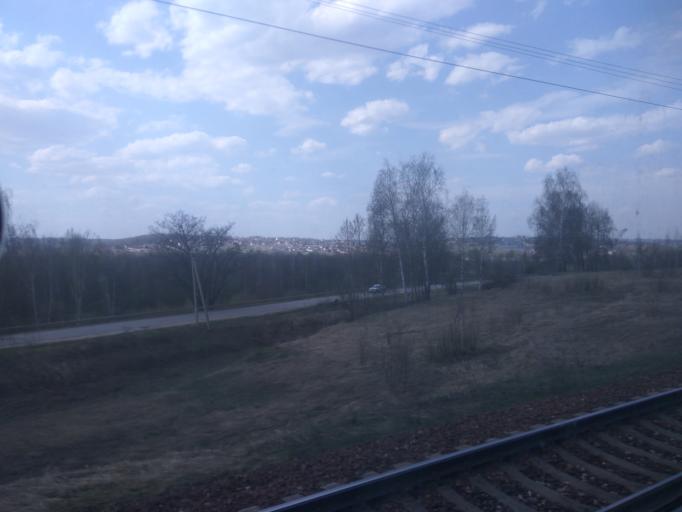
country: RU
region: Moskovskaya
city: Dedenevo
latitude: 56.2542
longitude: 37.5052
